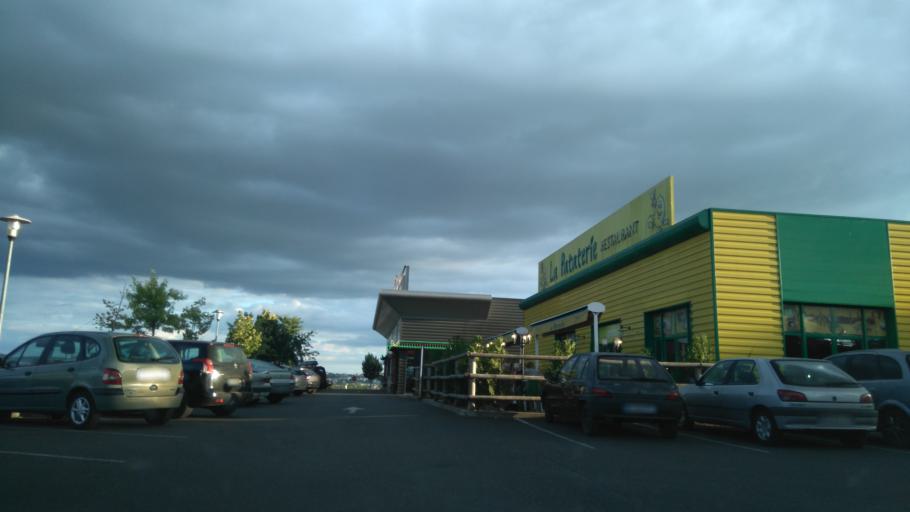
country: FR
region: Poitou-Charentes
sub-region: Departement de la Charente
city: Gond-Pontouvre
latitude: 45.6830
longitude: 0.1763
